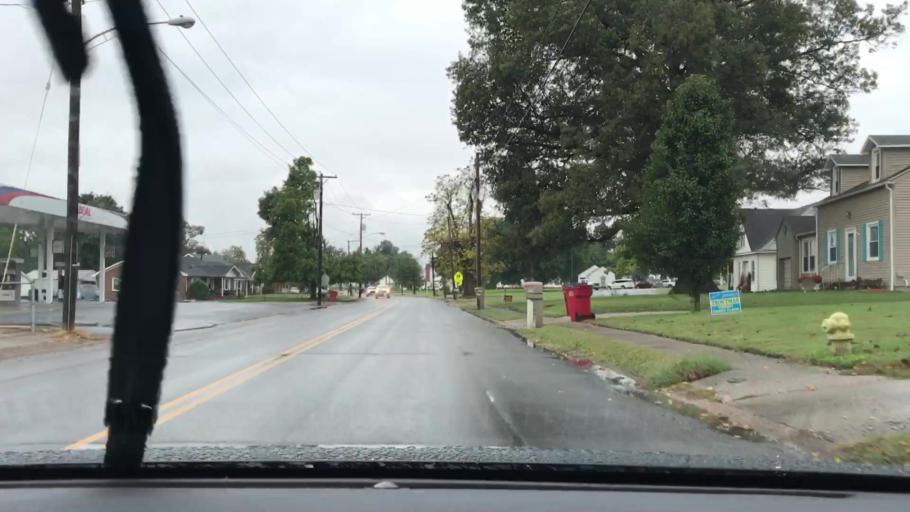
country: US
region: Kentucky
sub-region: McLean County
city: Calhoun
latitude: 37.5445
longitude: -87.2600
